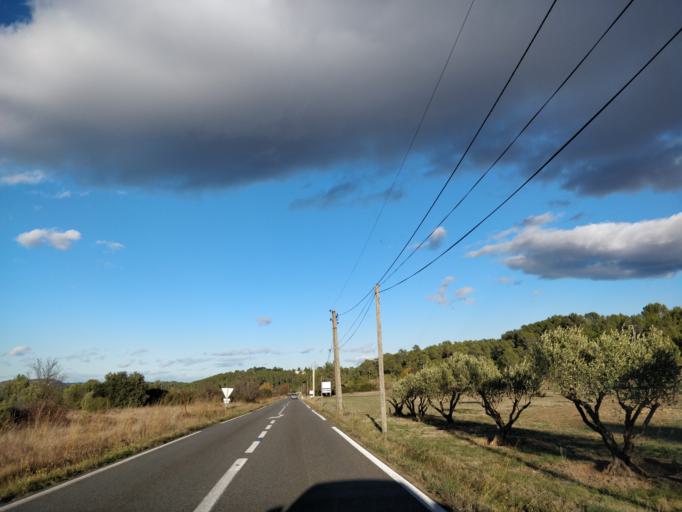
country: FR
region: Languedoc-Roussillon
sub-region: Departement de l'Herault
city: Saint-Drezery
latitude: 43.7233
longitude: 3.9551
